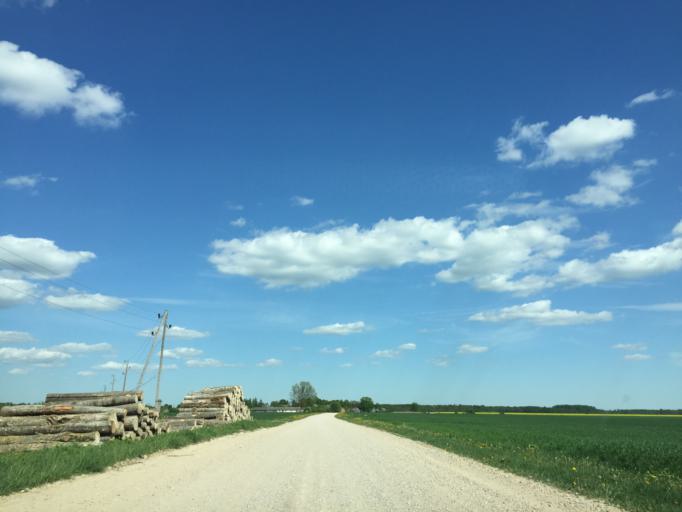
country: LV
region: Rundales
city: Pilsrundale
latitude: 56.3533
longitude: 23.9781
